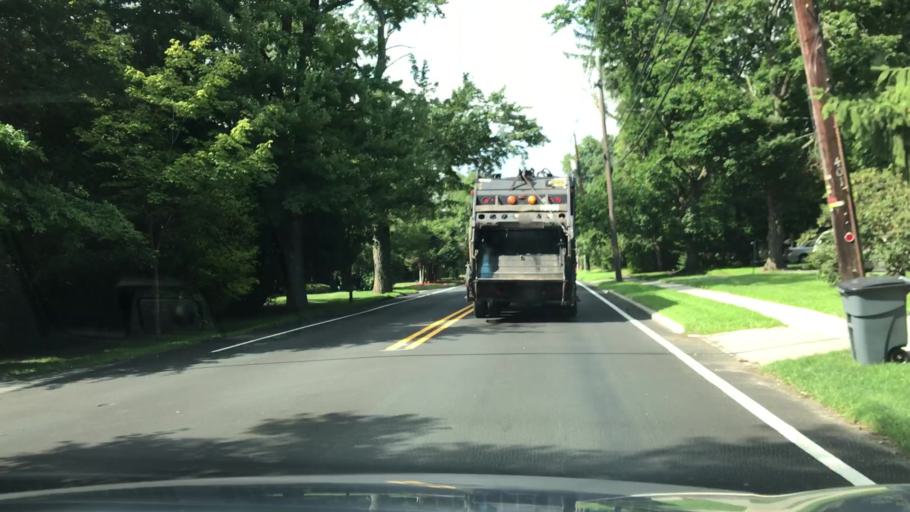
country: US
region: New Jersey
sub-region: Bergen County
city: Closter
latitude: 40.9679
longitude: -73.9740
